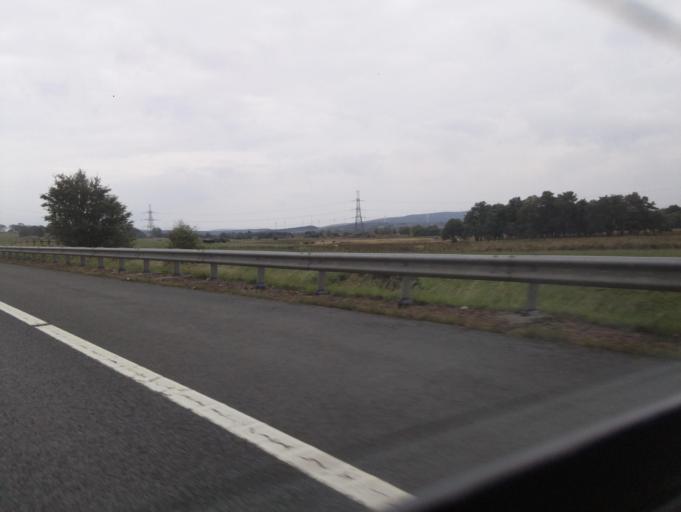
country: GB
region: Scotland
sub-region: South Lanarkshire
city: Lesmahagow
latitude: 55.6200
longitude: -3.8545
